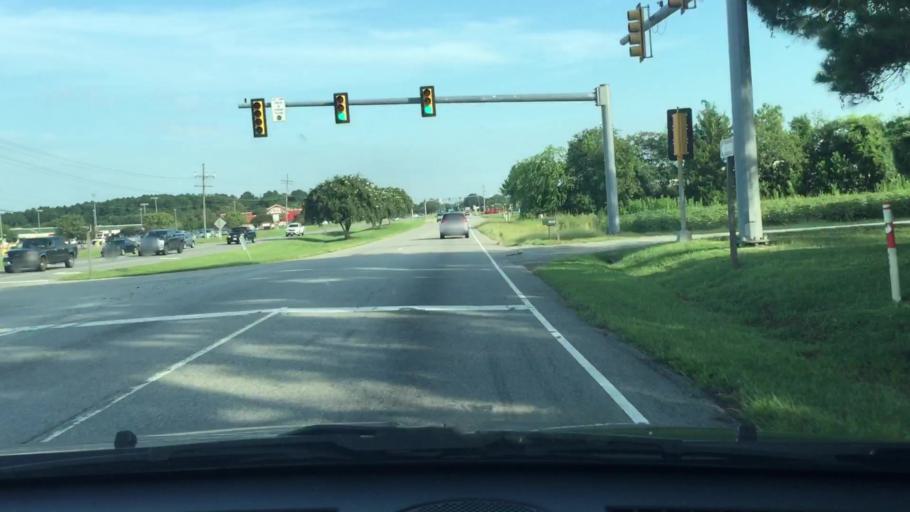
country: US
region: Virginia
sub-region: Isle of Wight County
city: Carrollton
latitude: 36.9545
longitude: -76.6008
